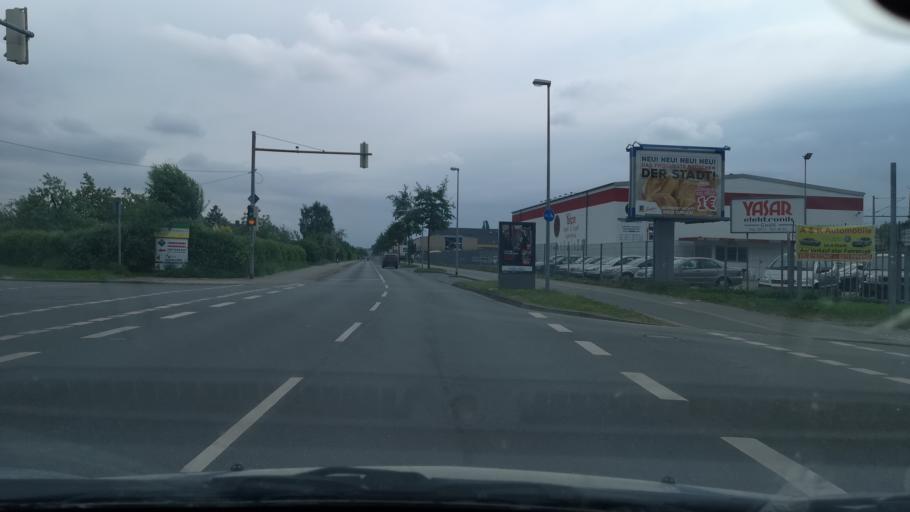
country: DE
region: Lower Saxony
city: Langenhagen
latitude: 52.4139
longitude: 9.6973
